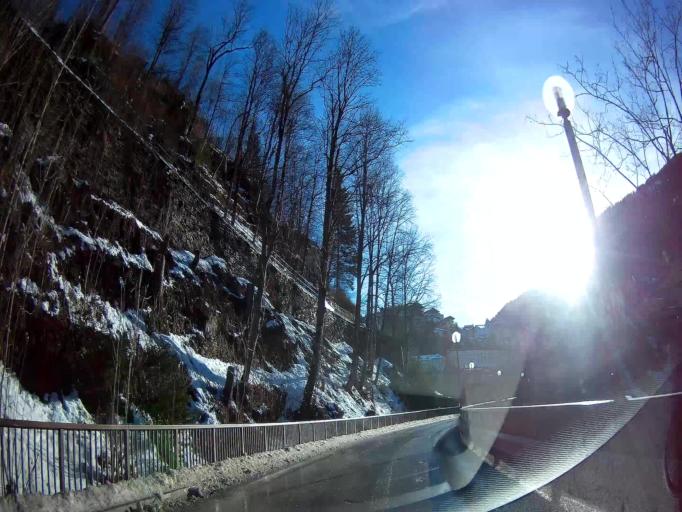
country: AT
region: Salzburg
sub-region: Politischer Bezirk Sankt Johann im Pongau
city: Bad Gastein
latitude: 47.1169
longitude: 13.1375
